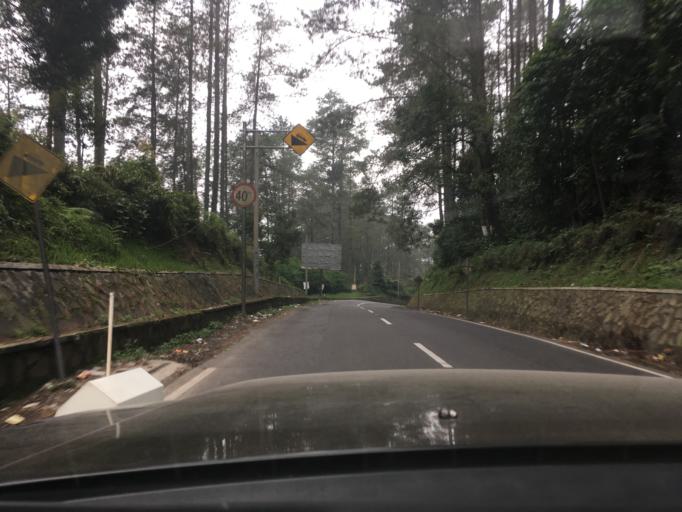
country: ID
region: West Java
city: Lembang
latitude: -6.7744
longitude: 107.6366
